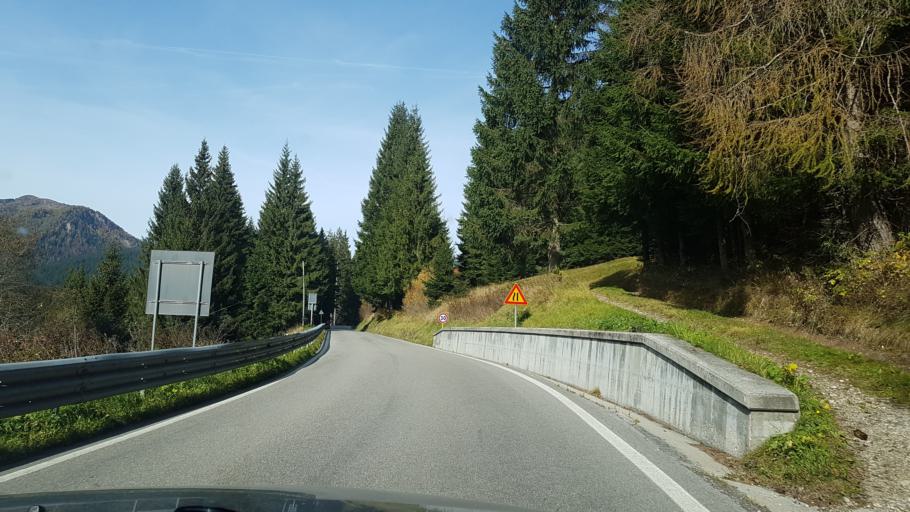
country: IT
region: Veneto
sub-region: Provincia di Belluno
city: Candide
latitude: 46.6238
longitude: 12.4704
